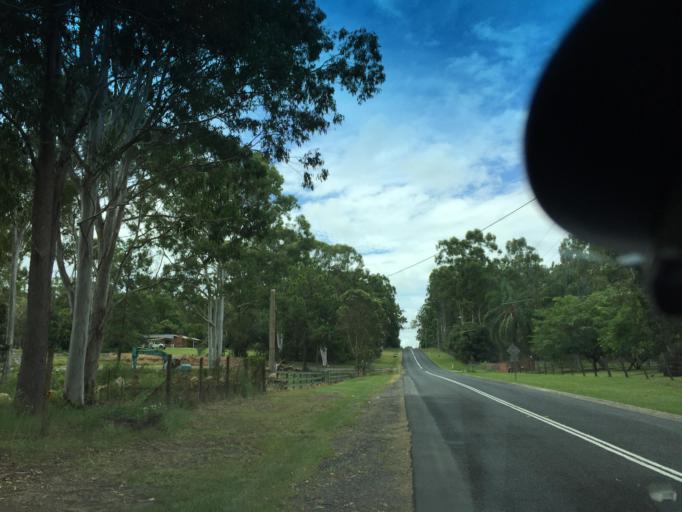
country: AU
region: Queensland
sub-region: Moreton Bay
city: Burpengary
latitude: -27.1452
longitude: 152.9617
